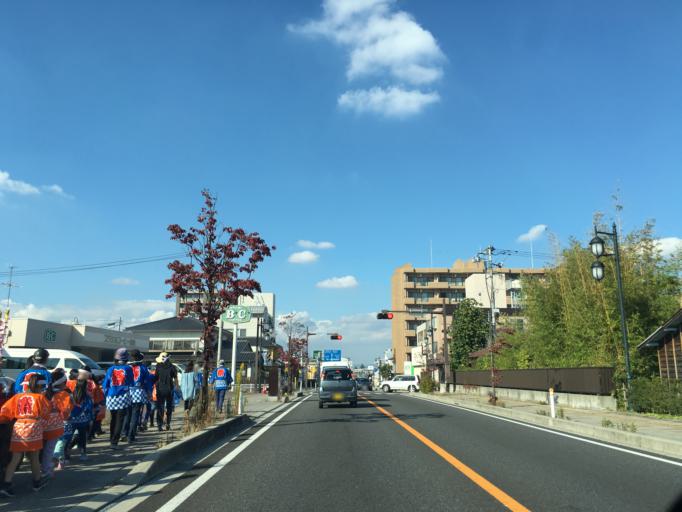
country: JP
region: Fukushima
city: Koriyama
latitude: 37.3893
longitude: 140.3552
